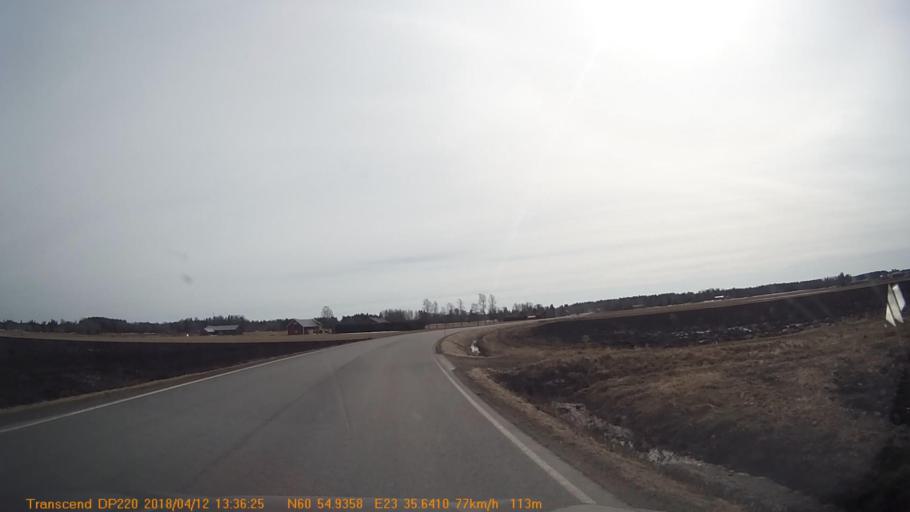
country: FI
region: Haeme
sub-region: Forssa
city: Forssa
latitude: 60.9153
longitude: 23.5942
